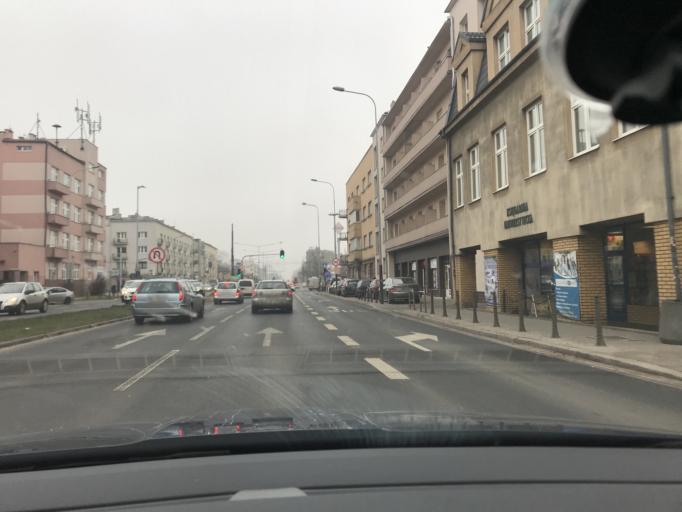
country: PL
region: Lodz Voivodeship
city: Lodz
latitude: 51.7741
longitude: 19.4824
